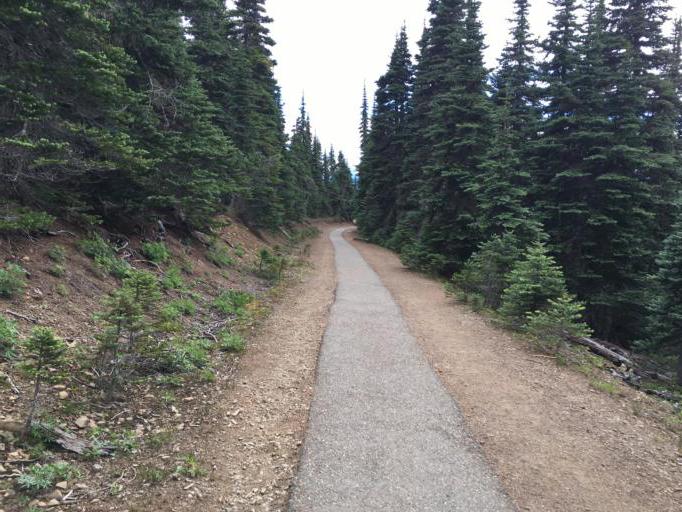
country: US
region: Washington
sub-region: Clallam County
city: Port Angeles
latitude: 47.9838
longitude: -123.5307
